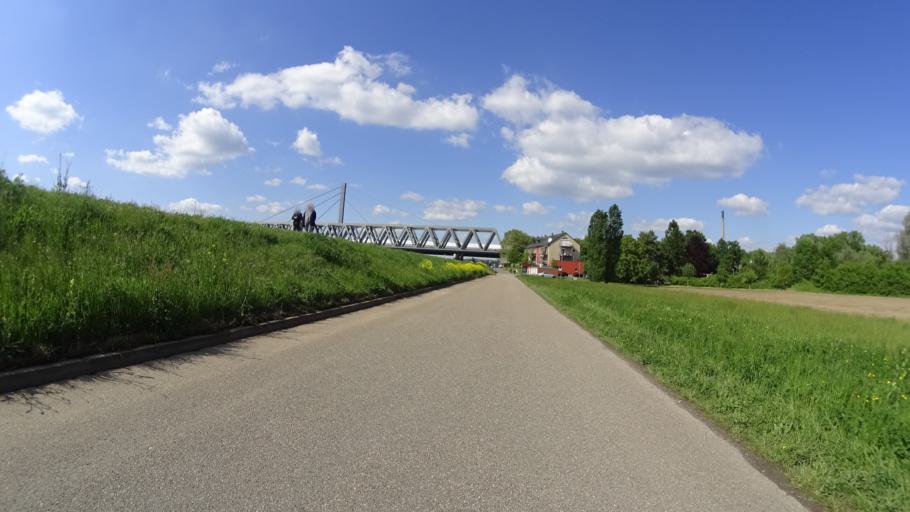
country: DE
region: Rheinland-Pfalz
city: Worth am Rhein
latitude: 49.0342
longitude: 8.3048
